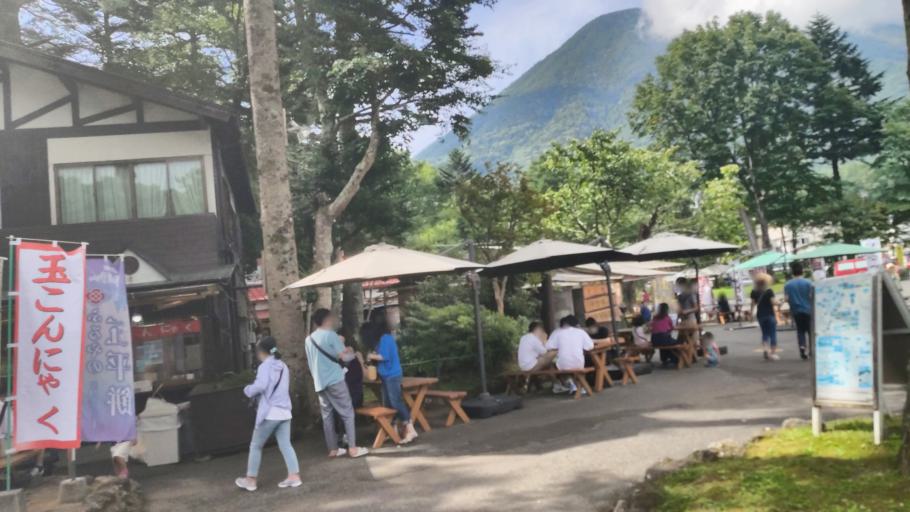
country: JP
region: Tochigi
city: Nikko
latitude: 36.7386
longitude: 139.5035
